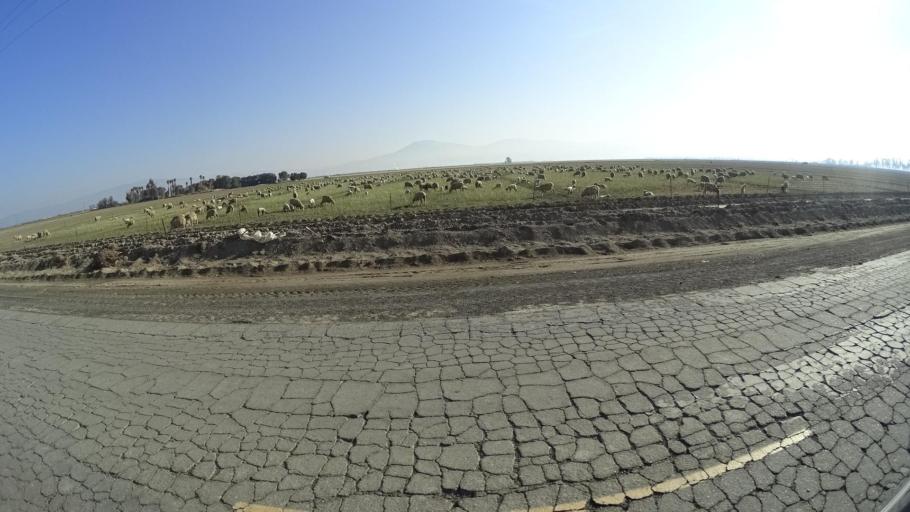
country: US
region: California
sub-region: Kern County
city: Weedpatch
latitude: 35.1966
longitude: -118.9680
